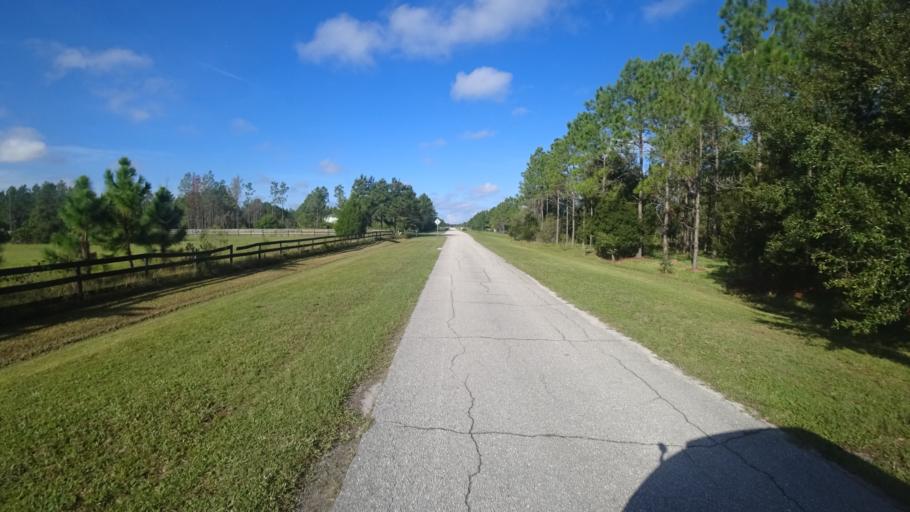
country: US
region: Florida
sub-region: Sarasota County
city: The Meadows
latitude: 27.4202
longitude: -82.3195
